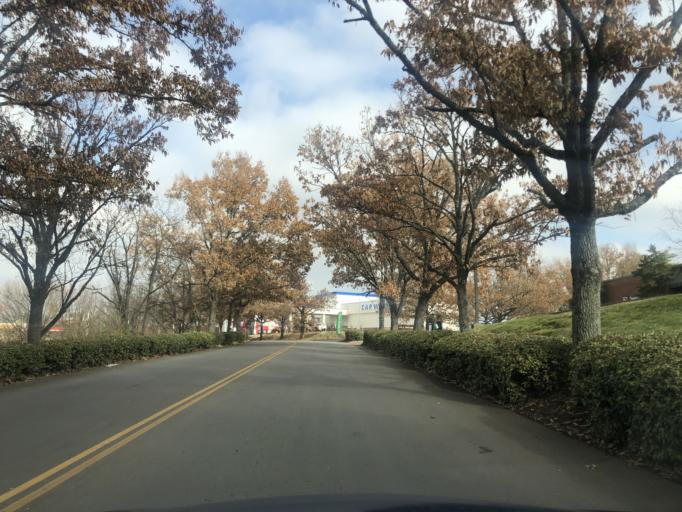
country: US
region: Tennessee
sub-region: Davidson County
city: Oak Hill
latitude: 36.0855
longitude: -86.6967
